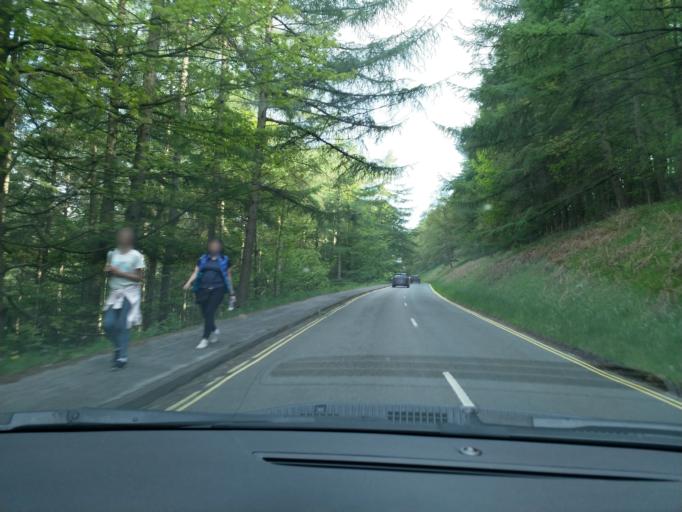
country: GB
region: England
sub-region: Derbyshire
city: Hope Valley
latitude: 53.3837
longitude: -1.7196
